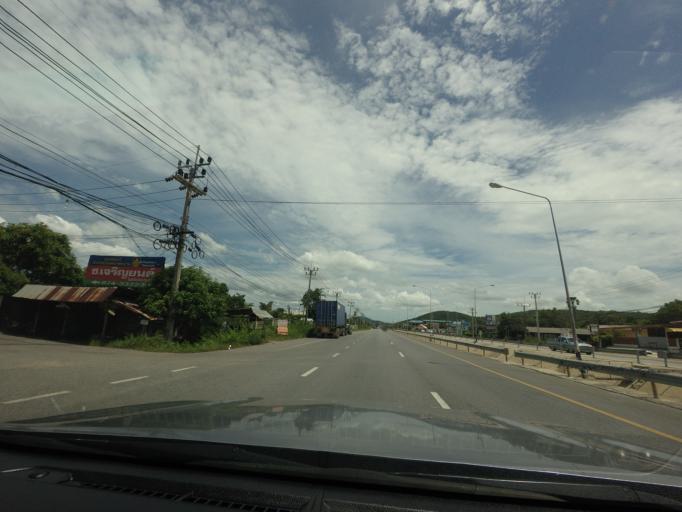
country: TH
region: Songkhla
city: Ban Mai
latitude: 7.2075
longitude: 100.5562
